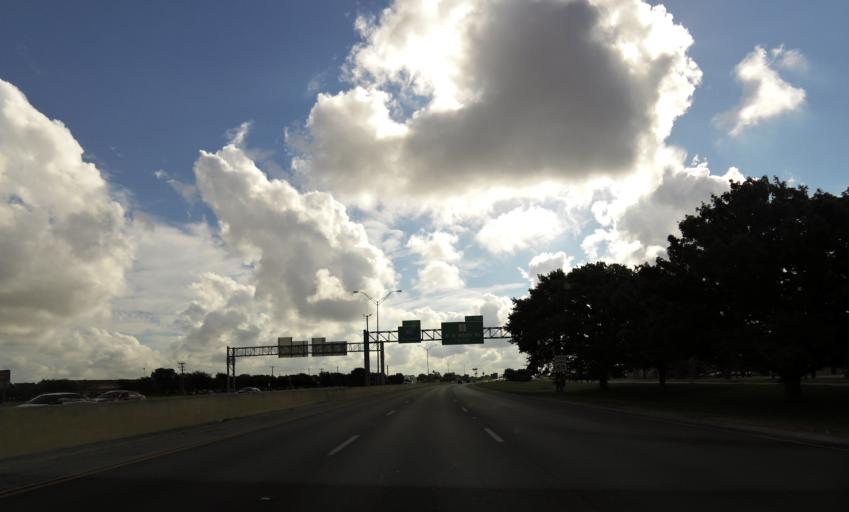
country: US
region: Texas
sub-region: Bexar County
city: Kirby
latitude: 29.4282
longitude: -98.4167
